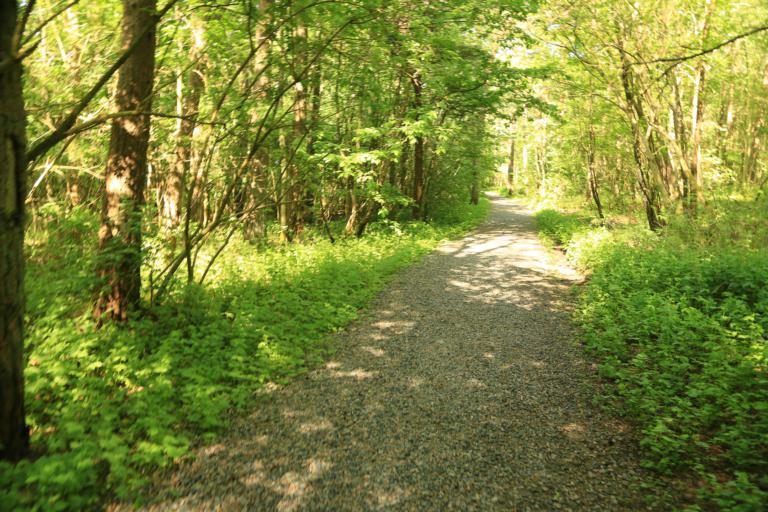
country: SE
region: Halland
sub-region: Varbergs Kommun
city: Varberg
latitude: 57.1072
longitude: 12.2863
